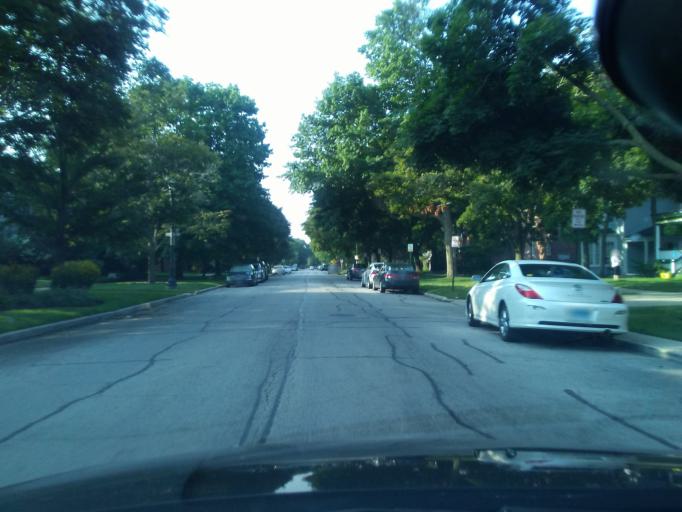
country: US
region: Illinois
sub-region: Cook County
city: Evanston
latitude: 42.0439
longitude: -87.6787
